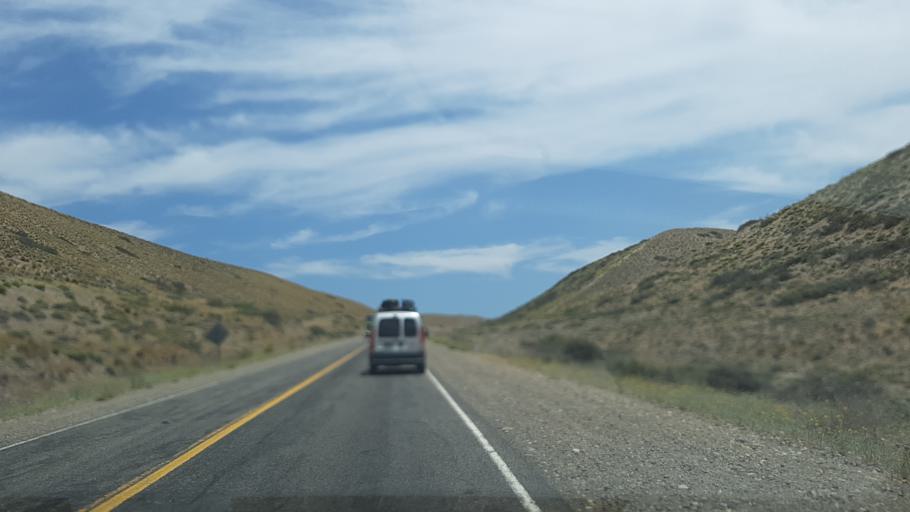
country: AR
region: Rio Negro
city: Pilcaniyeu
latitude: -40.4799
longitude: -70.6695
